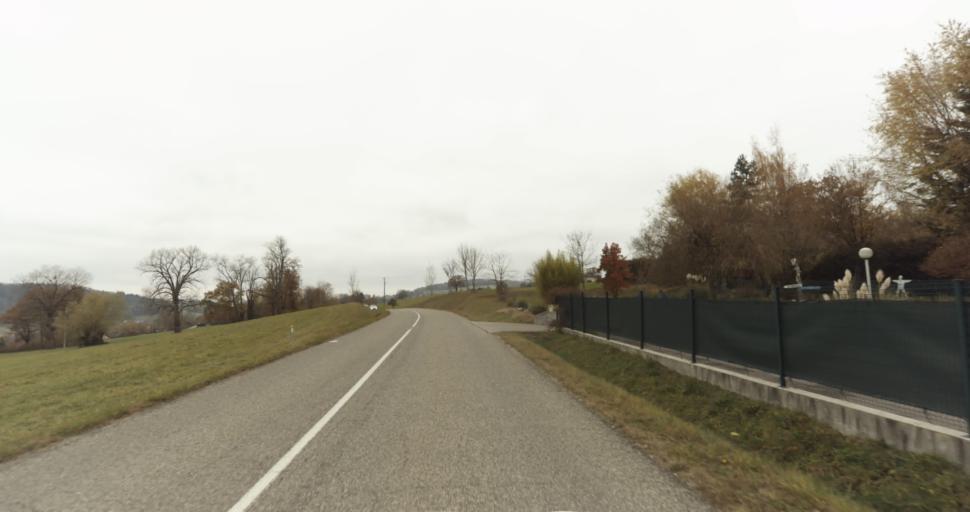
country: FR
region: Rhone-Alpes
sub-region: Departement de la Haute-Savoie
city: Alby-sur-Cheran
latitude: 45.8393
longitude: 6.0424
